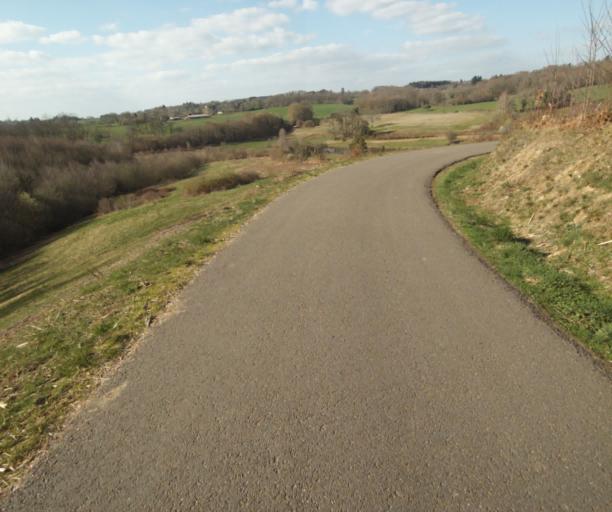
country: FR
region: Limousin
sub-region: Departement de la Correze
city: Saint-Mexant
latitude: 45.3194
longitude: 1.6191
